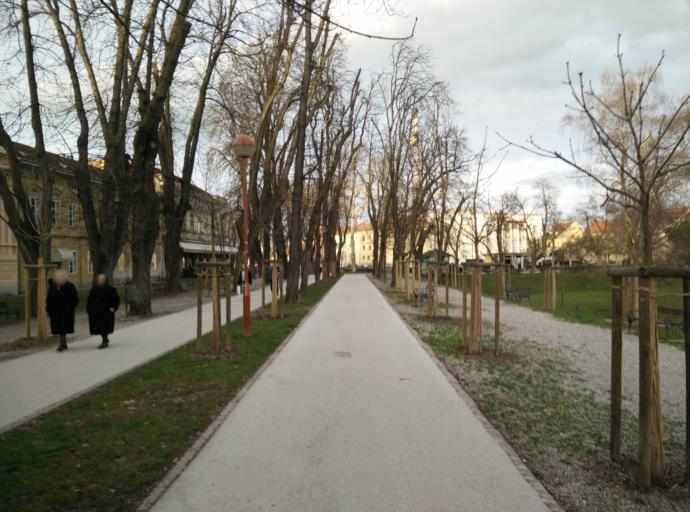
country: HR
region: Karlovacka
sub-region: Grad Karlovac
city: Karlovac
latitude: 45.4931
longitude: 15.5518
